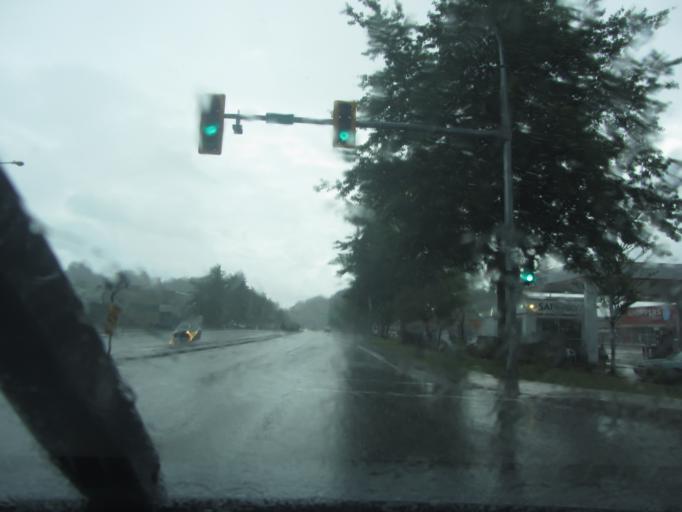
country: CA
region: British Columbia
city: Abbotsford
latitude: 49.1329
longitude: -122.3224
